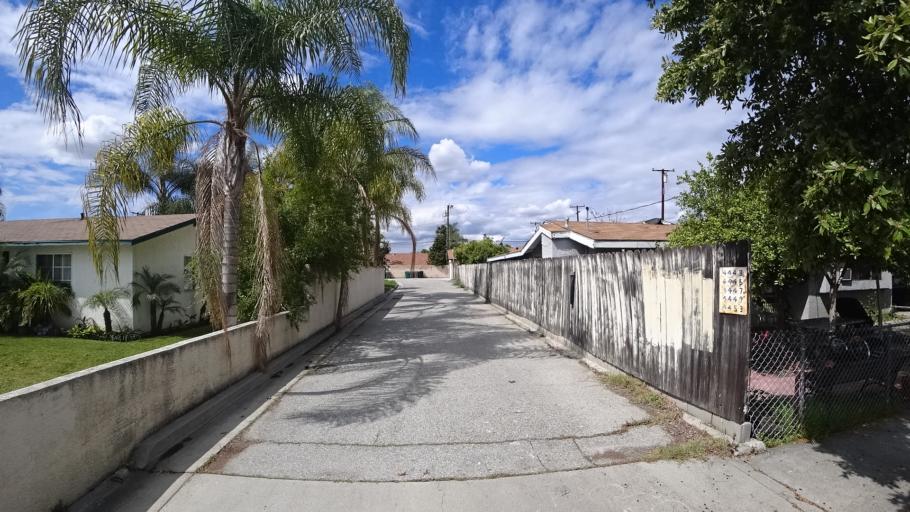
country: US
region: California
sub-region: Los Angeles County
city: Baldwin Park
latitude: 34.0938
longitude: -117.9671
